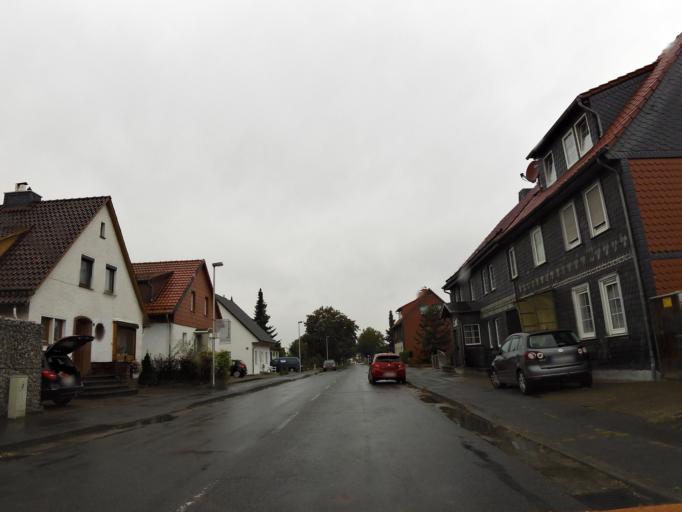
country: DE
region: Lower Saxony
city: Herzberg am Harz
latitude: 51.6305
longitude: 10.3694
